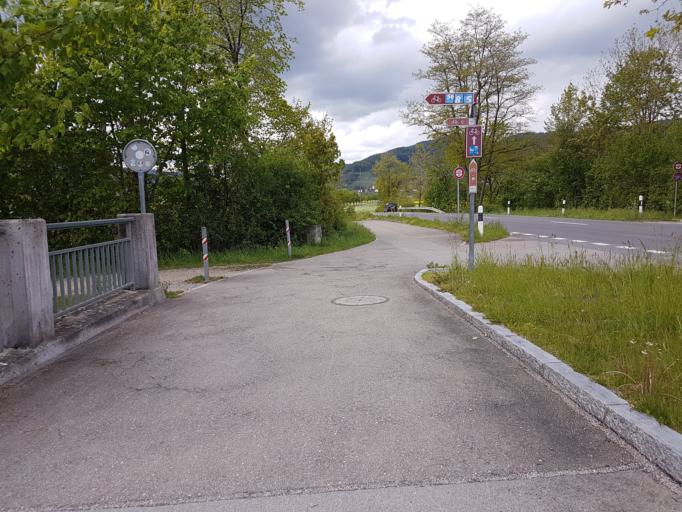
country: CH
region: Aargau
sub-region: Bezirk Brugg
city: Schinznach Bad
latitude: 47.4448
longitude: 8.1637
